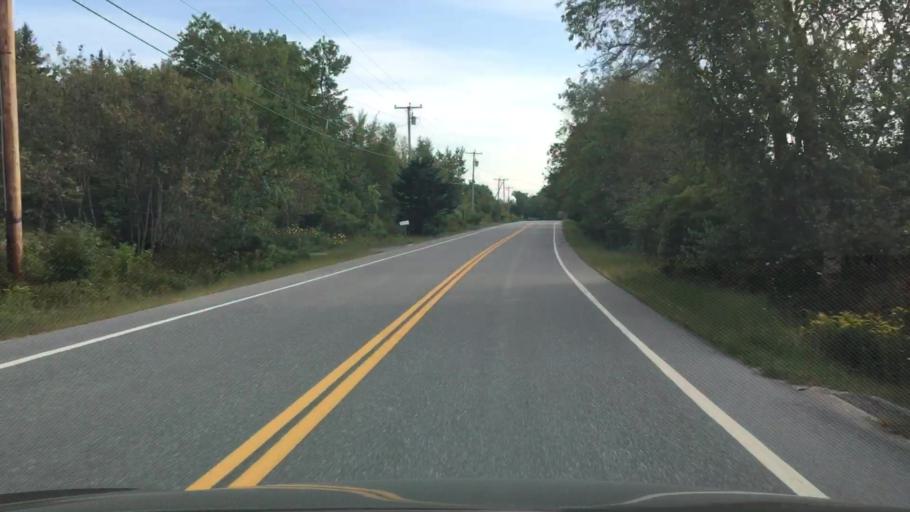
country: US
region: Maine
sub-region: Hancock County
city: Castine
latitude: 44.4424
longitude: -68.7877
